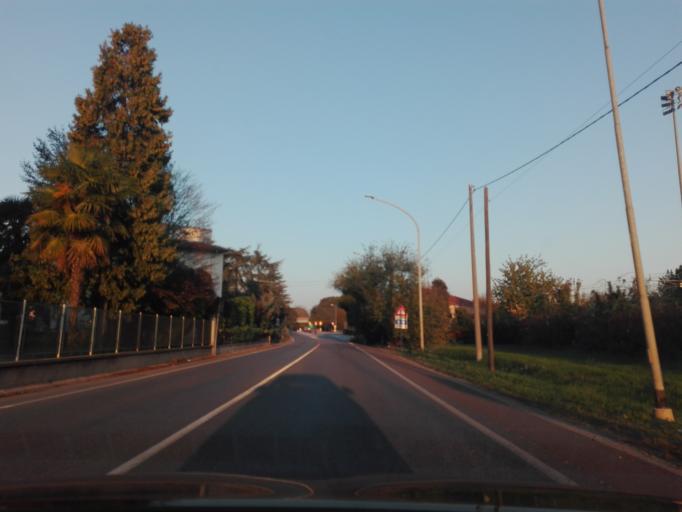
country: IT
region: Lombardy
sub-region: Provincia di Mantova
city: Mottella
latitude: 45.1524
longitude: 10.8351
